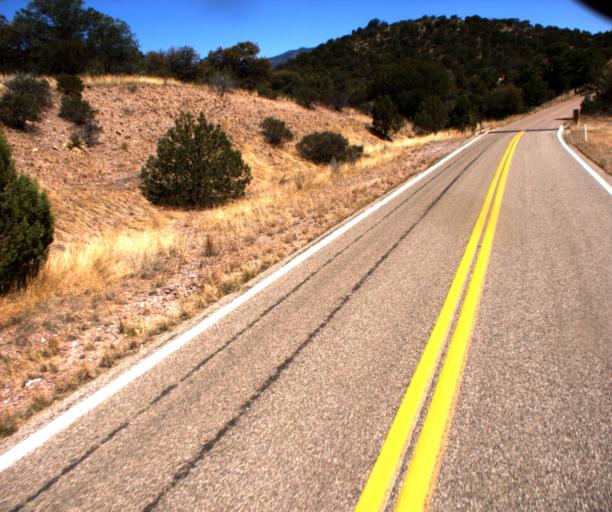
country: US
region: Arizona
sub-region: Cochise County
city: Sierra Vista
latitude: 31.4666
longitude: -110.4641
